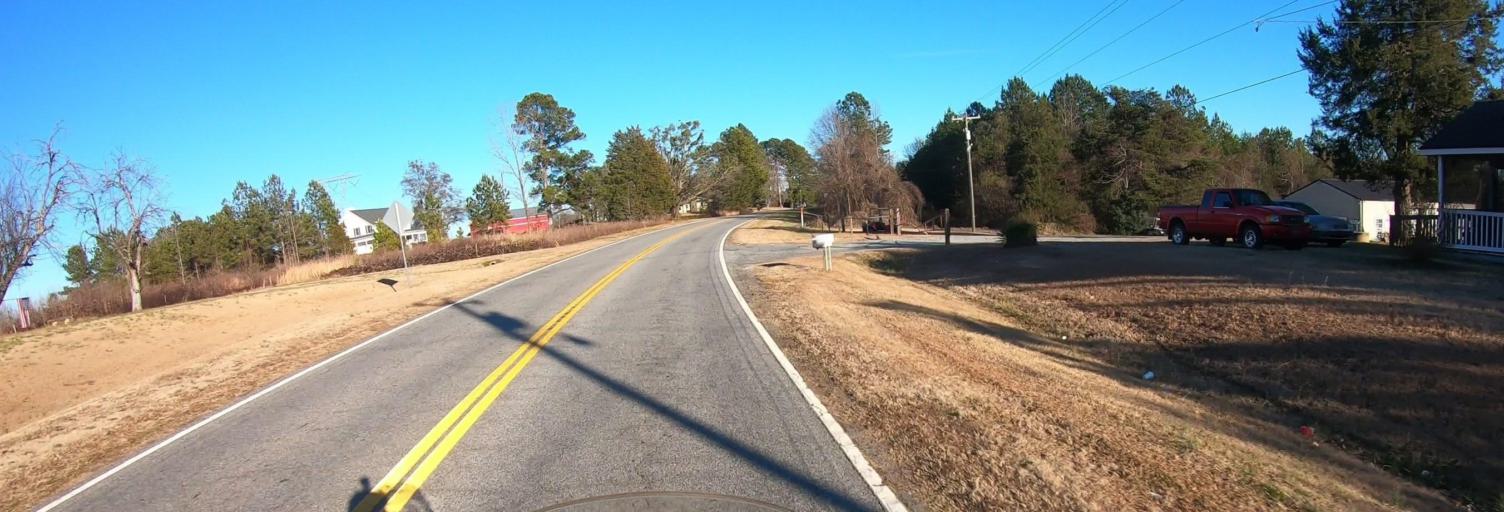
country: US
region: South Carolina
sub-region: Spartanburg County
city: Inman
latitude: 35.1408
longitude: -82.0991
